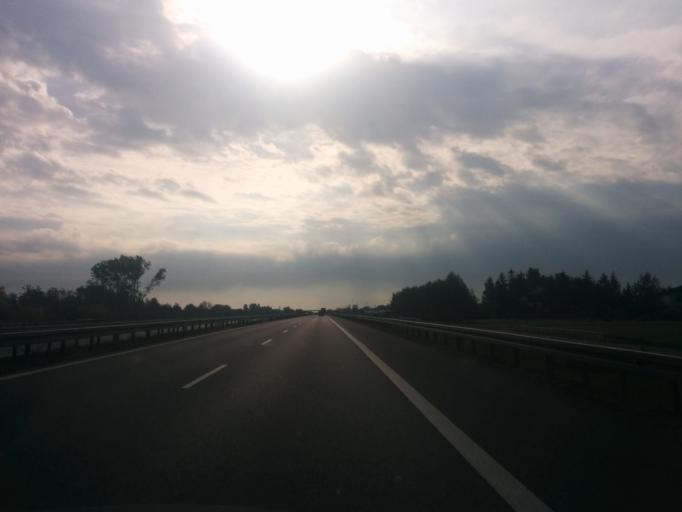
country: PL
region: Masovian Voivodeship
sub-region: Powiat bialobrzeski
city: Stara Blotnica
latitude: 51.5551
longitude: 21.0342
